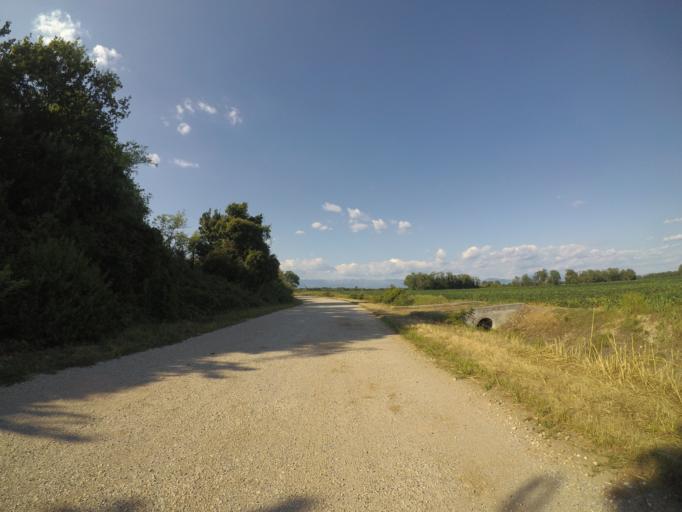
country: IT
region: Friuli Venezia Giulia
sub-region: Provincia di Udine
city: Pozzuolo del Friuli
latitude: 45.9986
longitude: 13.1790
